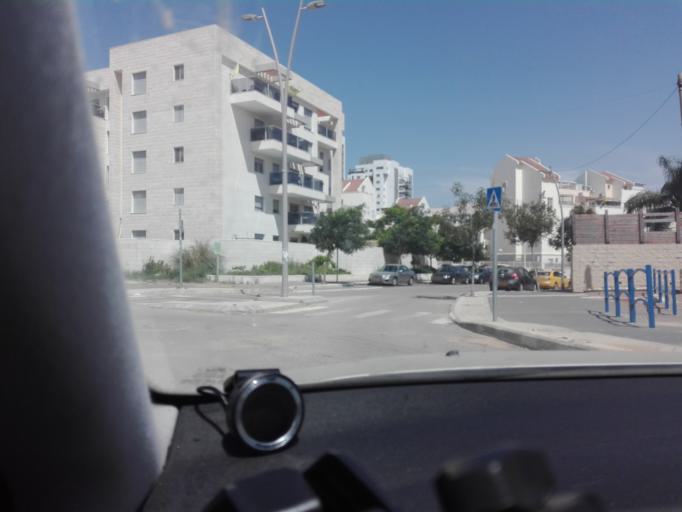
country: IL
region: Central District
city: Bene 'Ayish
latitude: 31.7275
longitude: 34.7372
